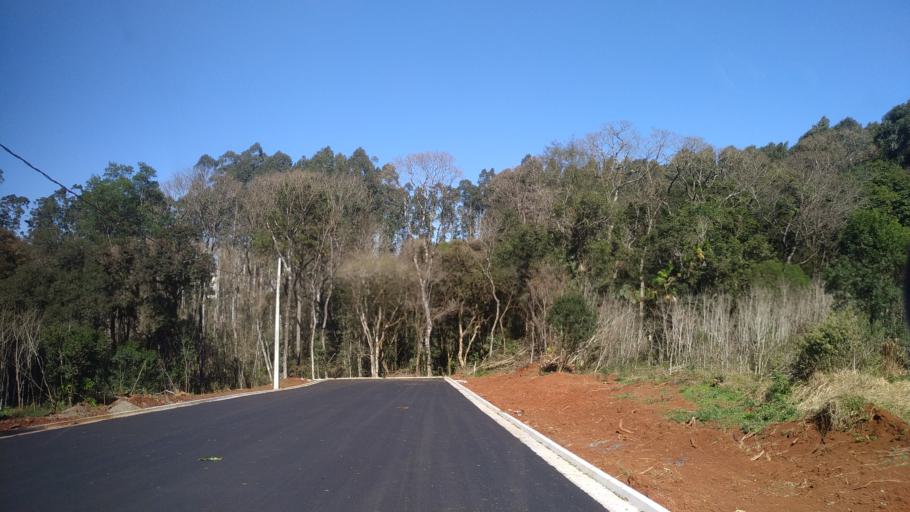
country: BR
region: Santa Catarina
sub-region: Chapeco
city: Chapeco
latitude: -27.0928
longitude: -52.7088
